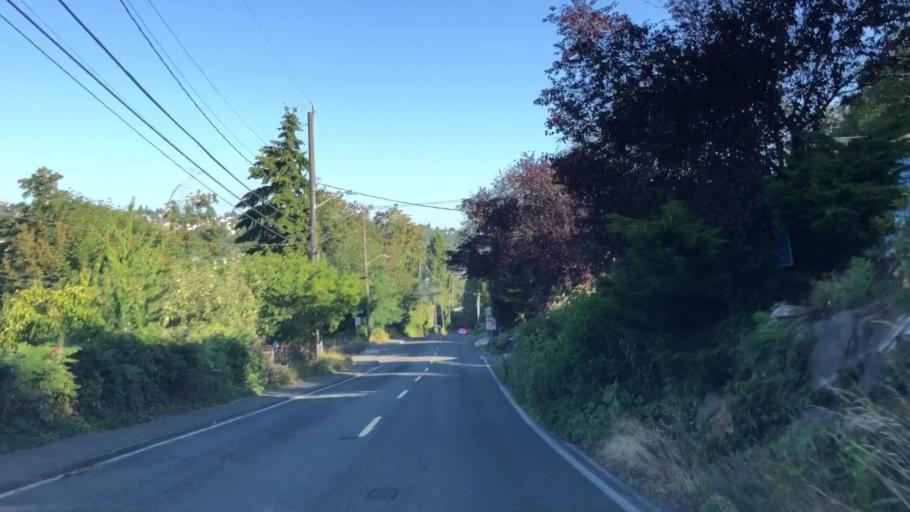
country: US
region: Washington
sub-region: King County
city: White Center
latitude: 47.5605
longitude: -122.3611
